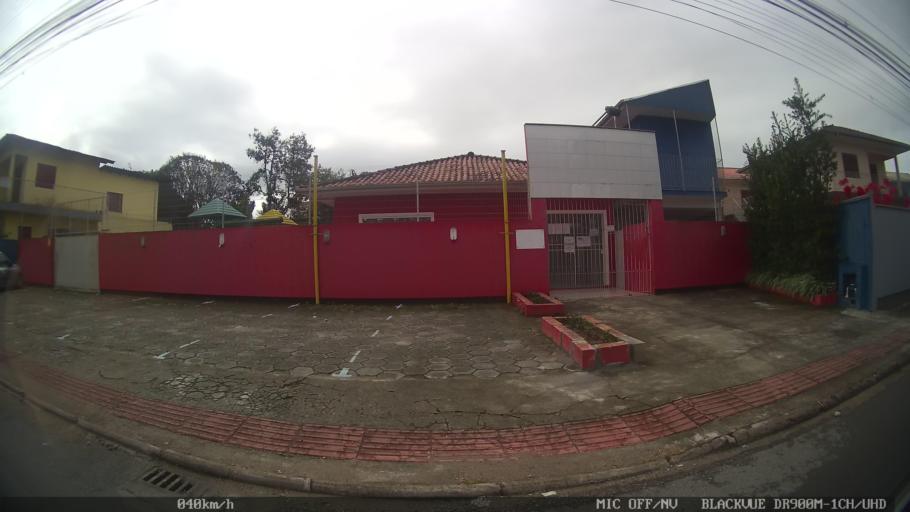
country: BR
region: Santa Catarina
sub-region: Biguacu
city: Biguacu
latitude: -27.5094
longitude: -48.6468
